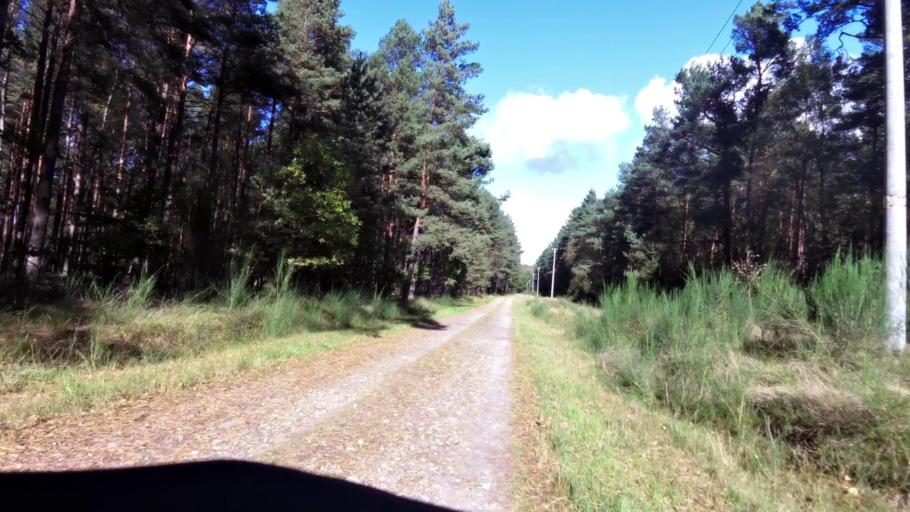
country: PL
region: West Pomeranian Voivodeship
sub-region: Powiat bialogardzki
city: Tychowo
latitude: 54.0231
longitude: 16.1480
